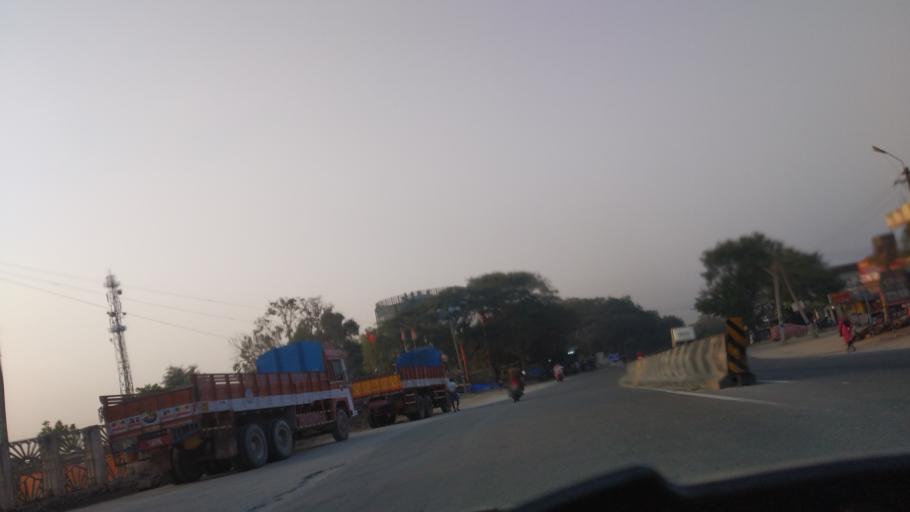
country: IN
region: Tamil Nadu
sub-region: Coimbatore
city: Madukkarai
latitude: 10.9106
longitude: 76.9488
